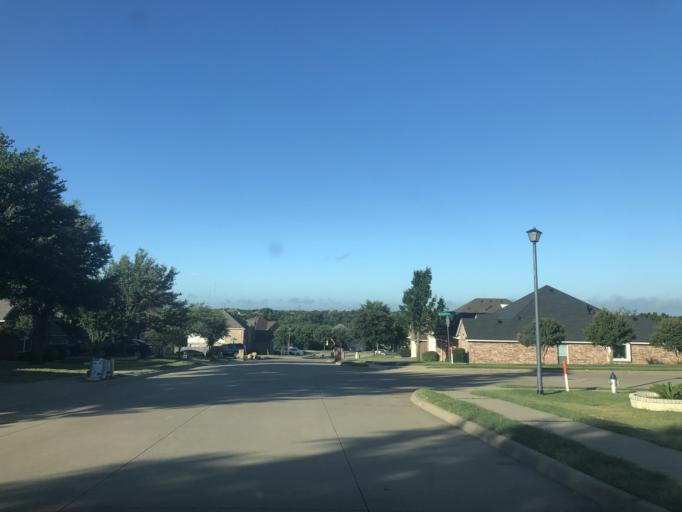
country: US
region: Texas
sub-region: Dallas County
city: Duncanville
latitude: 32.6579
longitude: -96.9471
